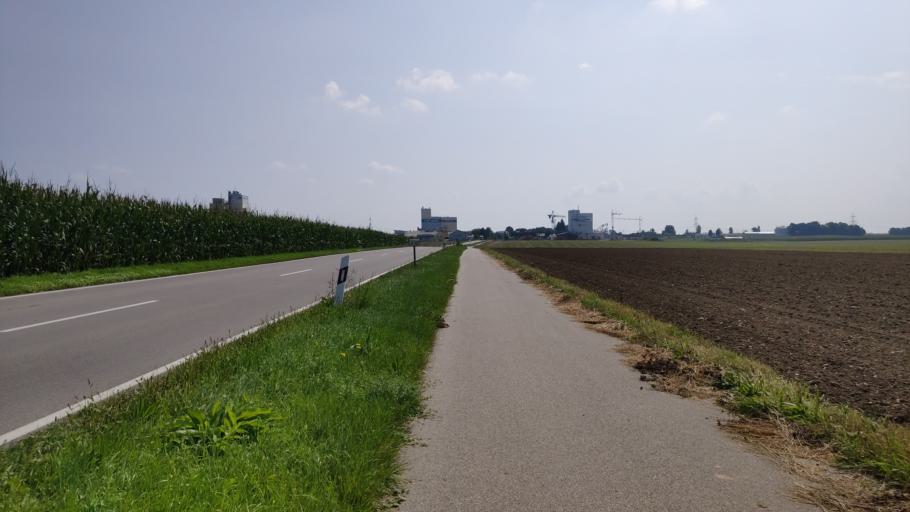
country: DE
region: Bavaria
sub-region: Swabia
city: Grossaitingen
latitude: 48.2258
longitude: 10.7926
